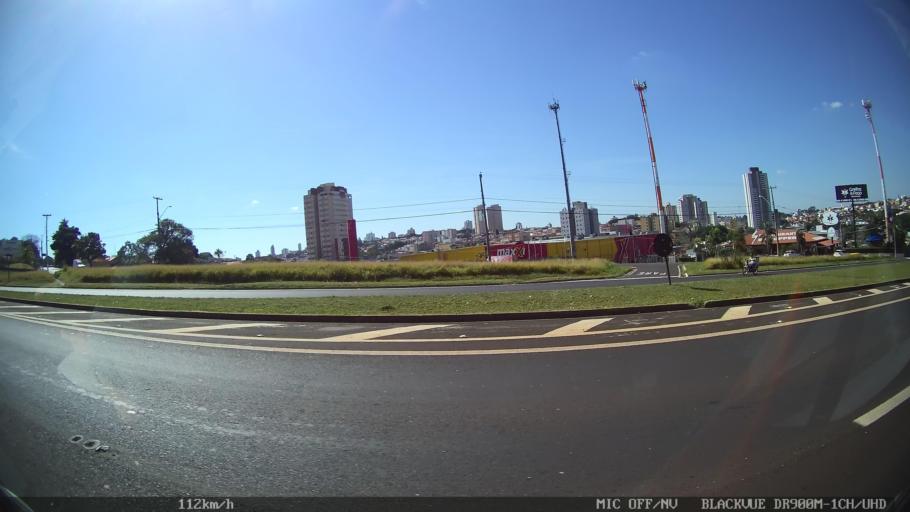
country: BR
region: Sao Paulo
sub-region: Franca
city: Franca
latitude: -20.5517
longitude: -47.4115
